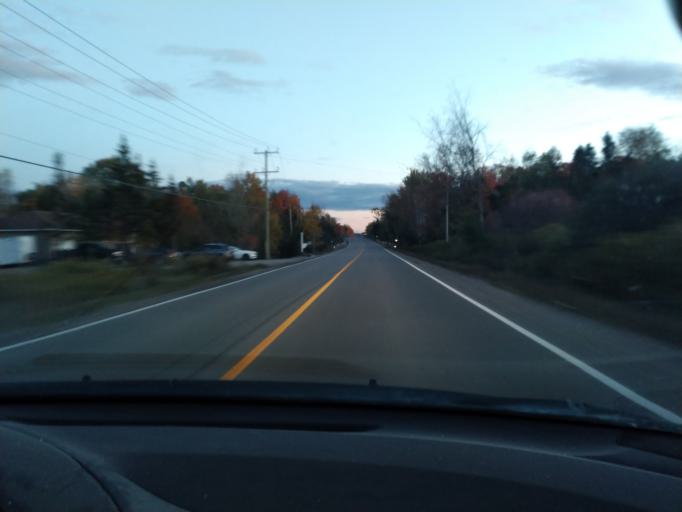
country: CA
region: Ontario
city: Innisfil
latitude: 44.2057
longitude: -79.6666
